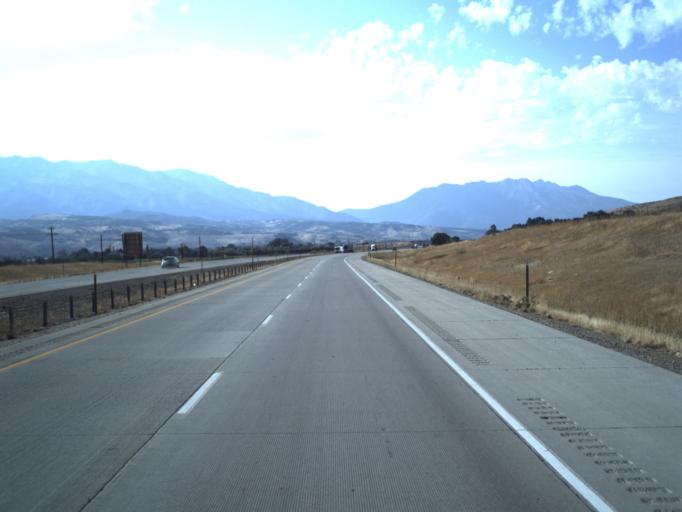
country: US
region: Utah
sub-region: Morgan County
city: Morgan
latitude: 41.0571
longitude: -111.6966
